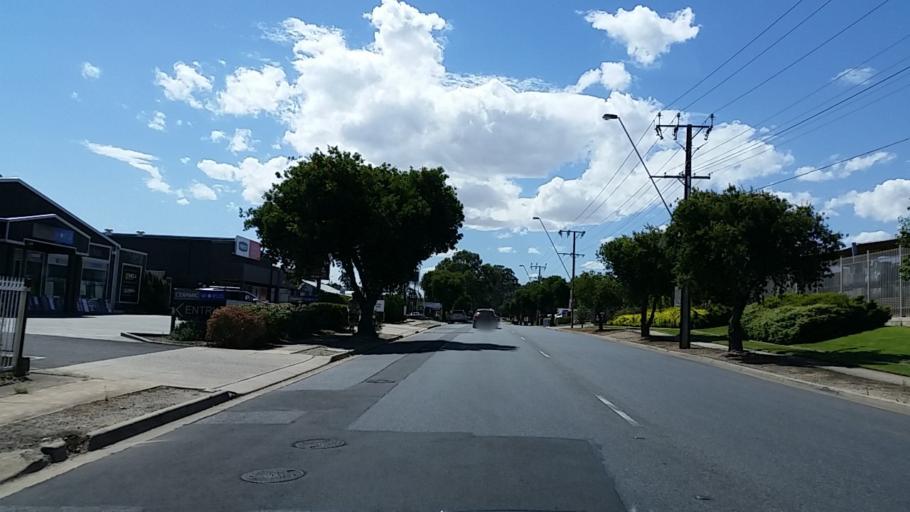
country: AU
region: South Australia
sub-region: Tea Tree Gully
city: Hope Valley
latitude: -34.8304
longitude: 138.7068
